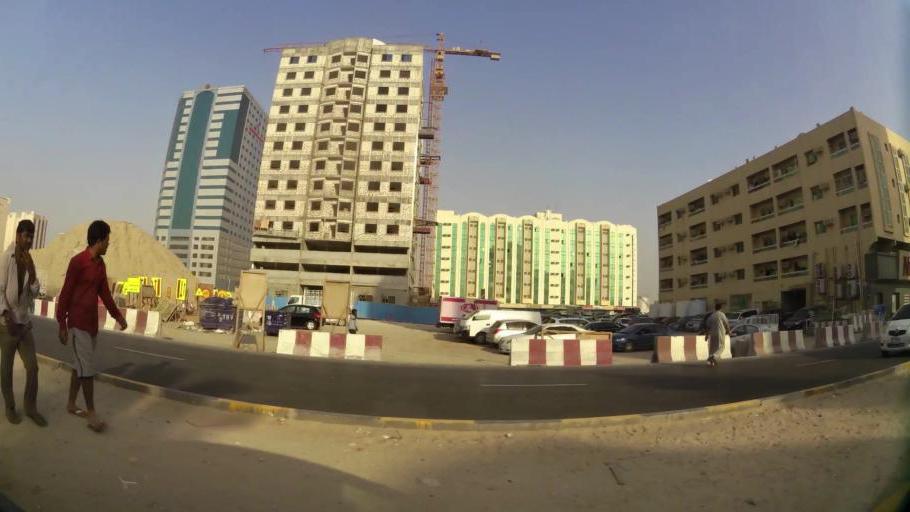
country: AE
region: Ajman
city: Ajman
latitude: 25.3778
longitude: 55.4562
